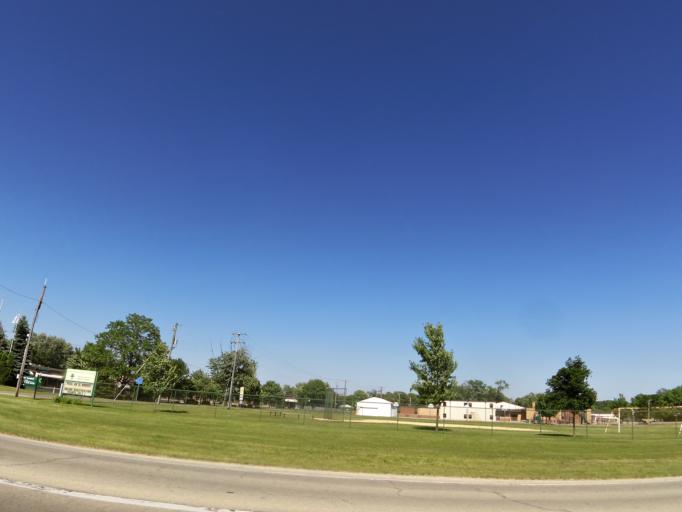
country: US
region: Illinois
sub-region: Winnebago County
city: Roscoe
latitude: 42.4205
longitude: -89.0141
